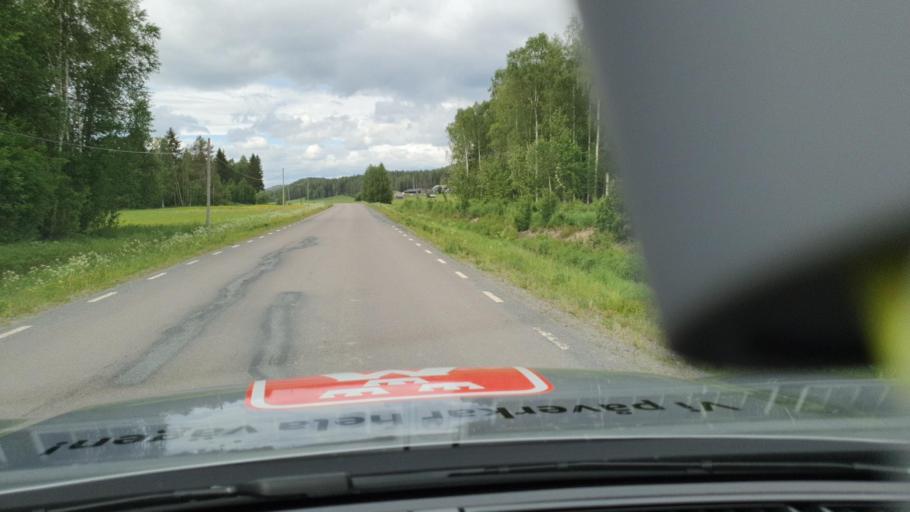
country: SE
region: Norrbotten
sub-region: Lulea Kommun
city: Sodra Sunderbyn
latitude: 65.8556
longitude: 21.9214
